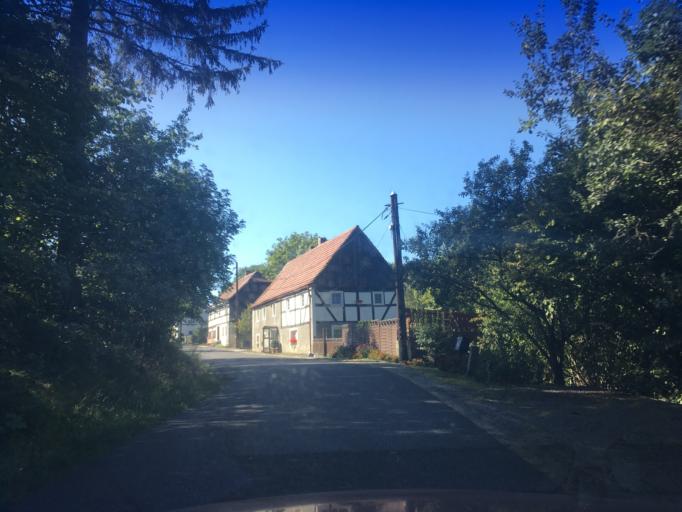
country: PL
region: Lower Silesian Voivodeship
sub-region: Powiat lubanski
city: Lesna
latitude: 51.0094
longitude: 15.1946
